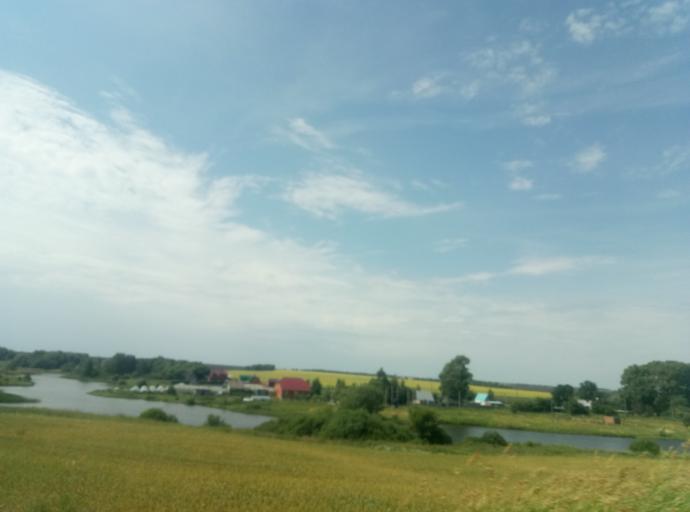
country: RU
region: Tula
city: Kireyevsk
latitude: 53.9042
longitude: 37.9786
